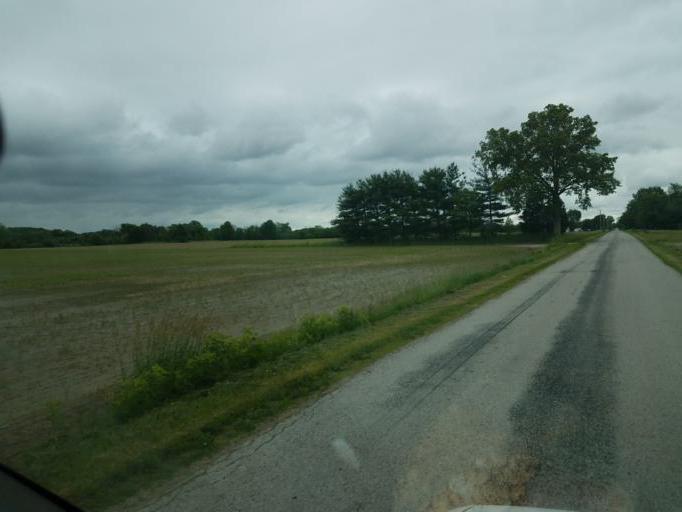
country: US
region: Ohio
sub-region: Morrow County
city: Cardington
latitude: 40.5510
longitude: -82.9194
